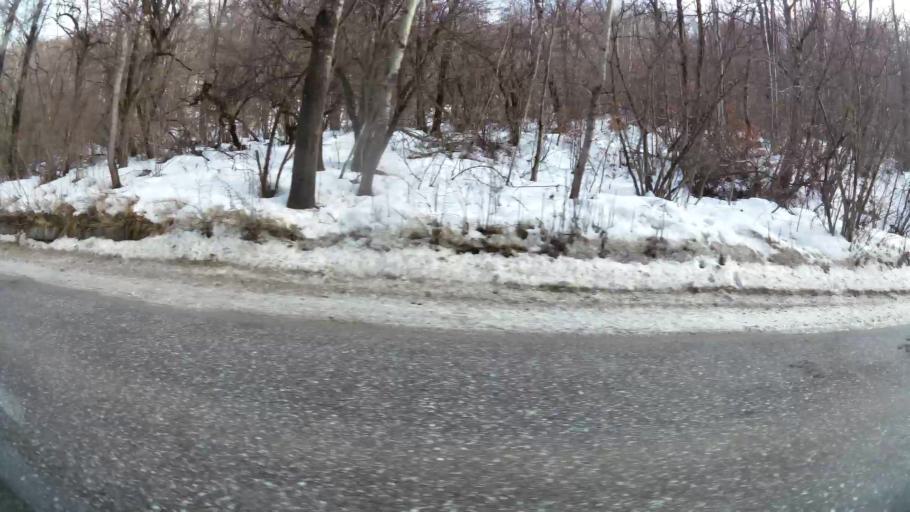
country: BG
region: Sofia-Capital
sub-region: Stolichna Obshtina
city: Sofia
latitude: 42.6312
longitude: 23.2301
